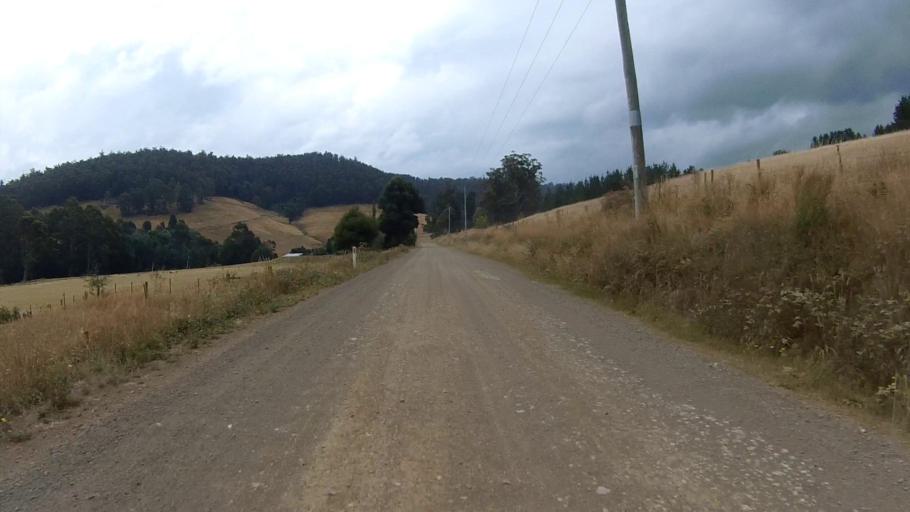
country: AU
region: Tasmania
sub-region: Huon Valley
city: Huonville
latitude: -42.9738
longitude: 147.0542
